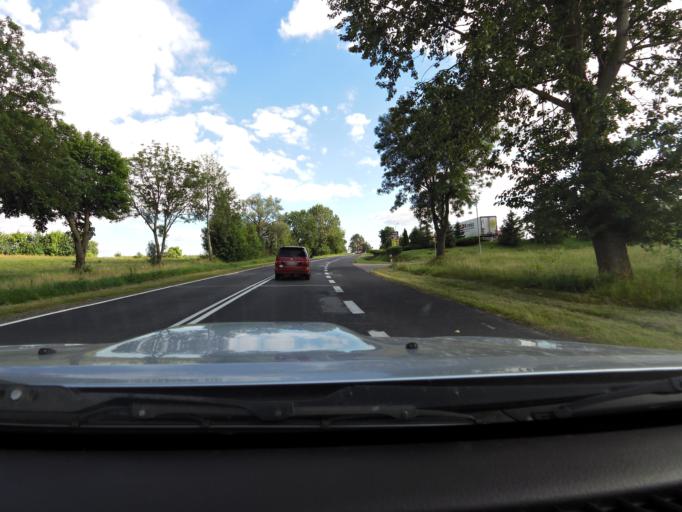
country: PL
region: Podlasie
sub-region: Powiat grajewski
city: Rajgrod
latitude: 53.8696
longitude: 22.6780
